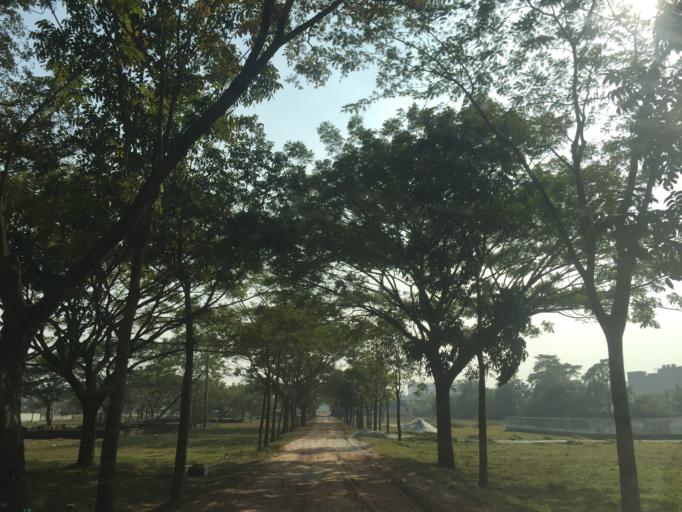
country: BD
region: Dhaka
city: Tungi
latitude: 23.8724
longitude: 90.3129
